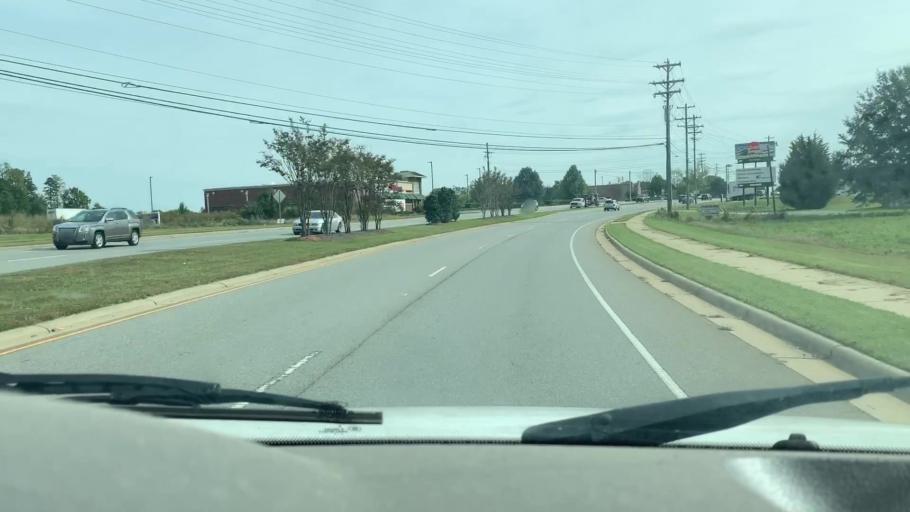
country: US
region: North Carolina
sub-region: Catawba County
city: Lake Norman of Catawba
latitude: 35.5689
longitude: -80.9049
